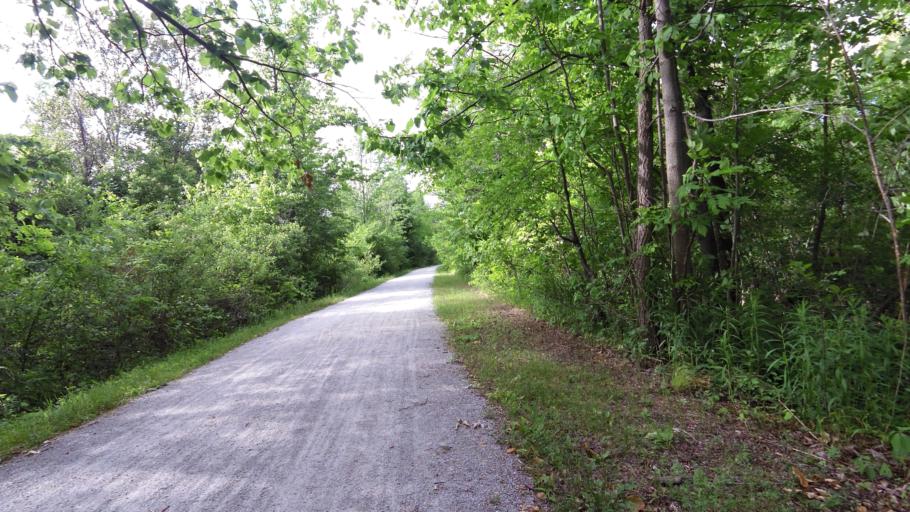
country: CA
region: Ontario
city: Orangeville
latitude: 43.8073
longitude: -79.9326
